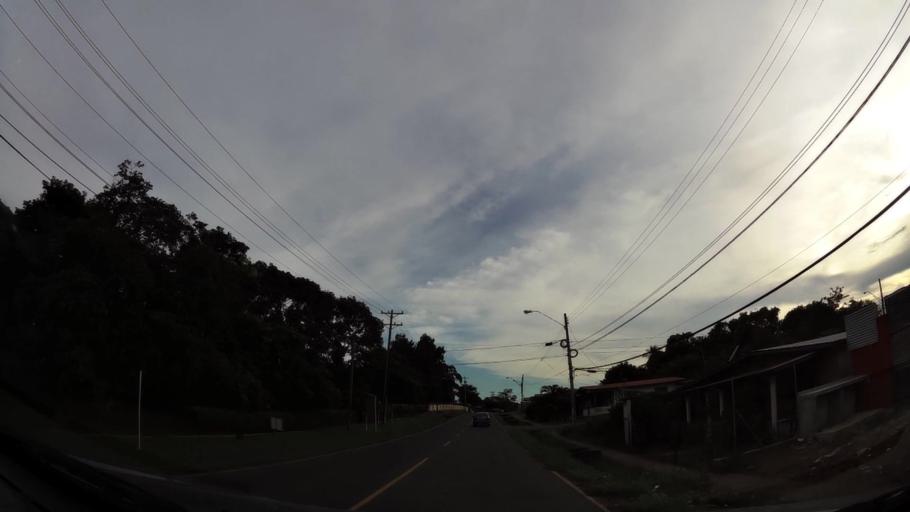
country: PA
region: Panama
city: La Chorrera
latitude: 8.8918
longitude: -79.7785
